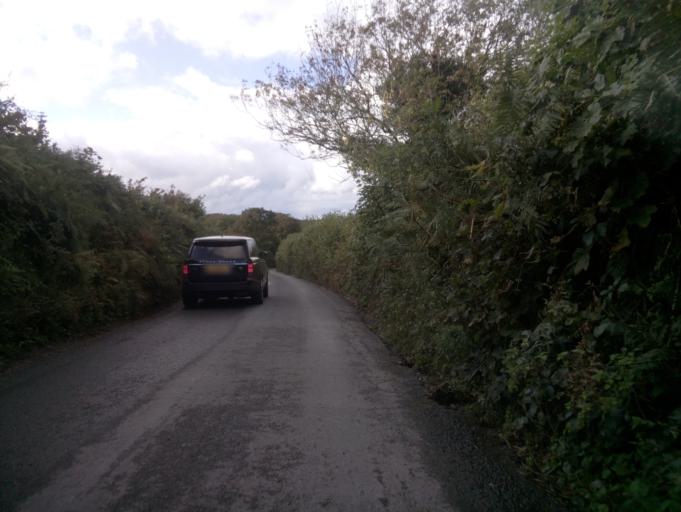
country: GB
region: England
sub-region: Devon
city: South Brent
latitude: 50.3993
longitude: -3.7807
